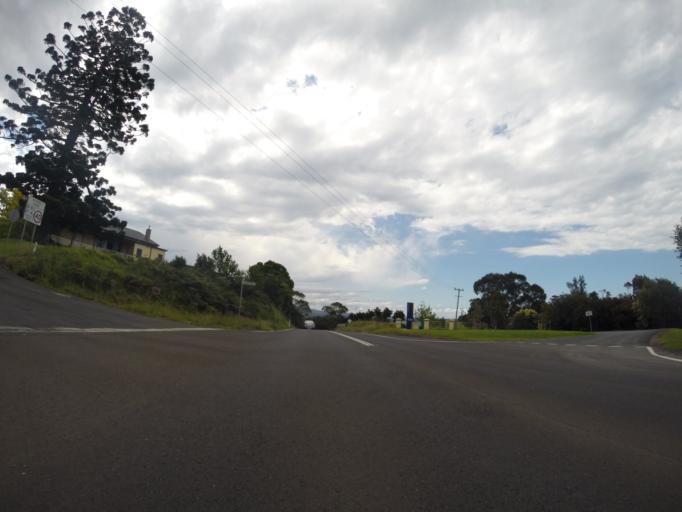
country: AU
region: New South Wales
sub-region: Shoalhaven Shire
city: Milton
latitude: -35.3118
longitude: 150.4321
